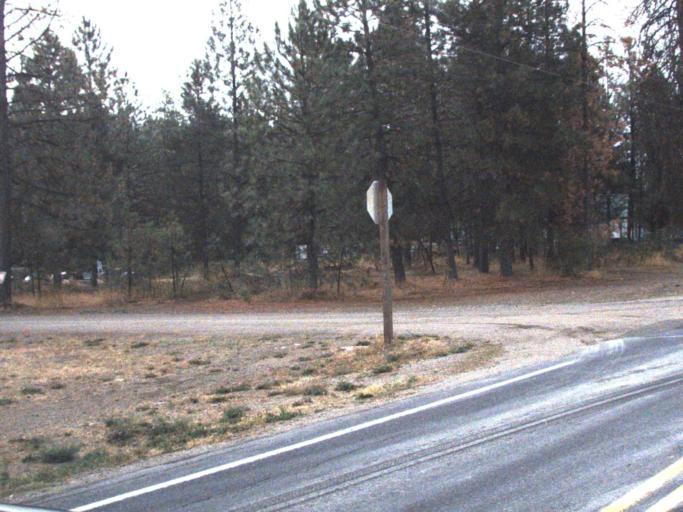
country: US
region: Washington
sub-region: Stevens County
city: Chewelah
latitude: 48.0538
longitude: -117.7415
